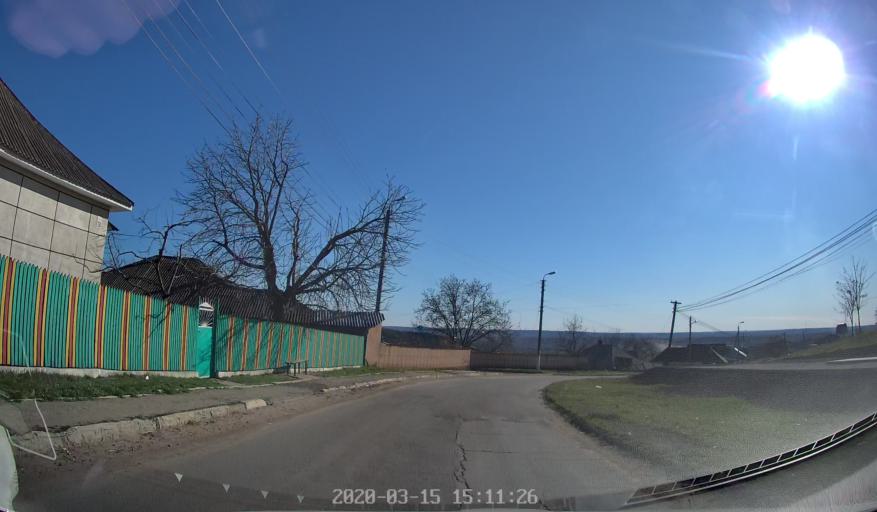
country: MD
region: Orhei
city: Orhei
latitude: 47.2625
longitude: 28.7773
